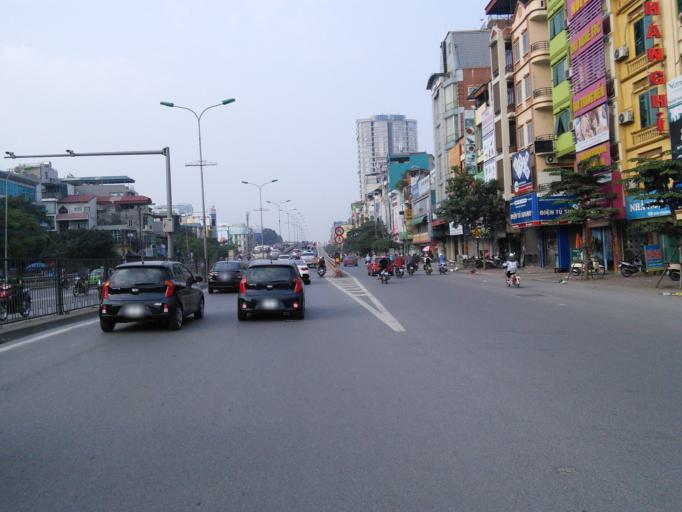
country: VN
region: Ha Noi
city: Hai BaTrung
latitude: 20.9952
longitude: 105.8412
